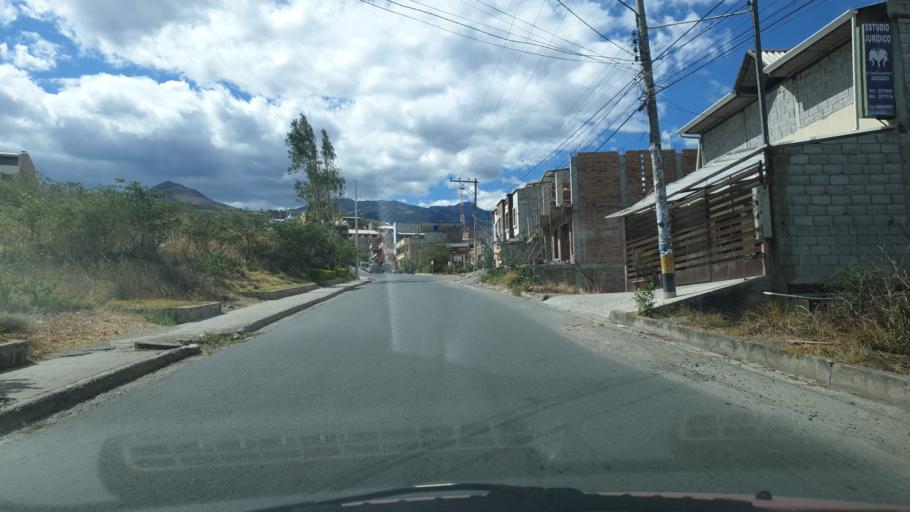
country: EC
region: Azuay
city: Cuenca
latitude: -3.2789
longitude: -79.3136
